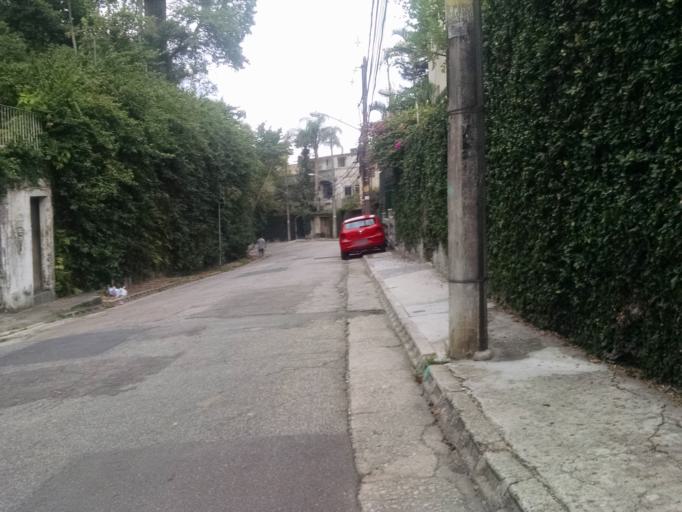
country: BR
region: Rio de Janeiro
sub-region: Rio De Janeiro
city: Rio de Janeiro
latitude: -22.9347
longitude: -43.1964
